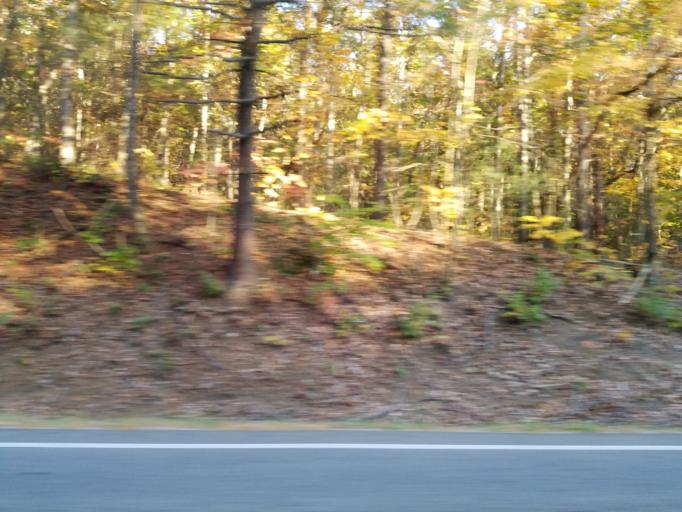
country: US
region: Georgia
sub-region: Pickens County
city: Jasper
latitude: 34.5754
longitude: -84.3028
